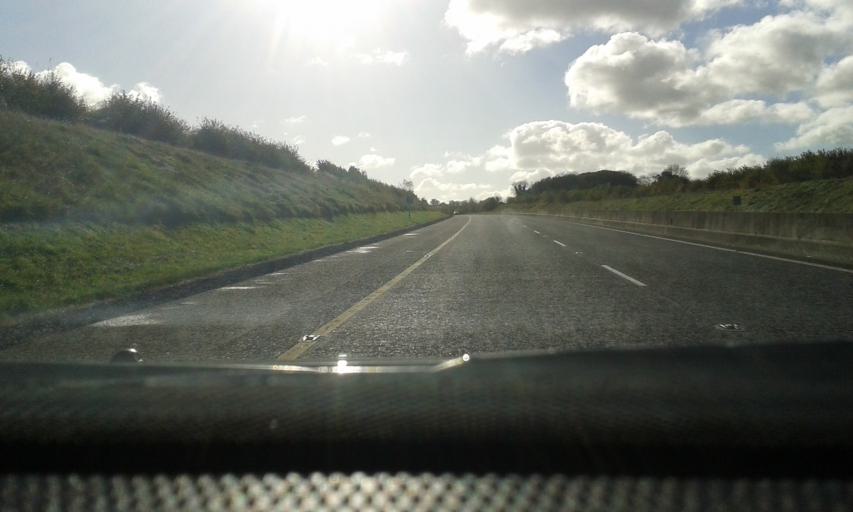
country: IE
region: Munster
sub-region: County Cork
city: Rathcormac
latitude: 52.0729
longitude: -8.3028
